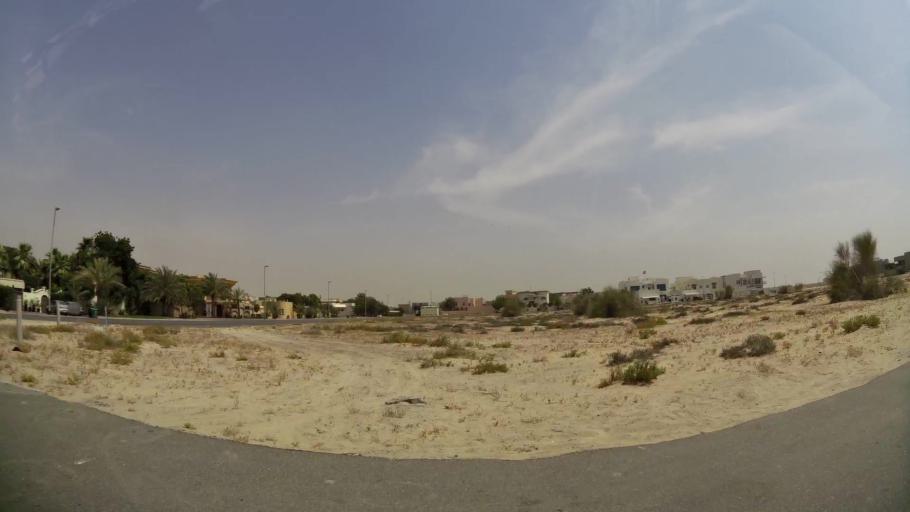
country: AE
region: Ash Shariqah
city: Sharjah
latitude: 25.2420
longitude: 55.4213
